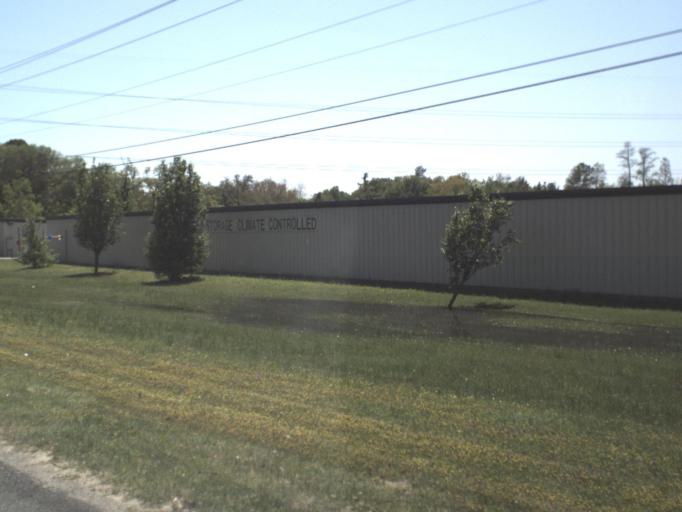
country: US
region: Florida
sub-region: Escambia County
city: Bellview
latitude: 30.4721
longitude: -87.3066
